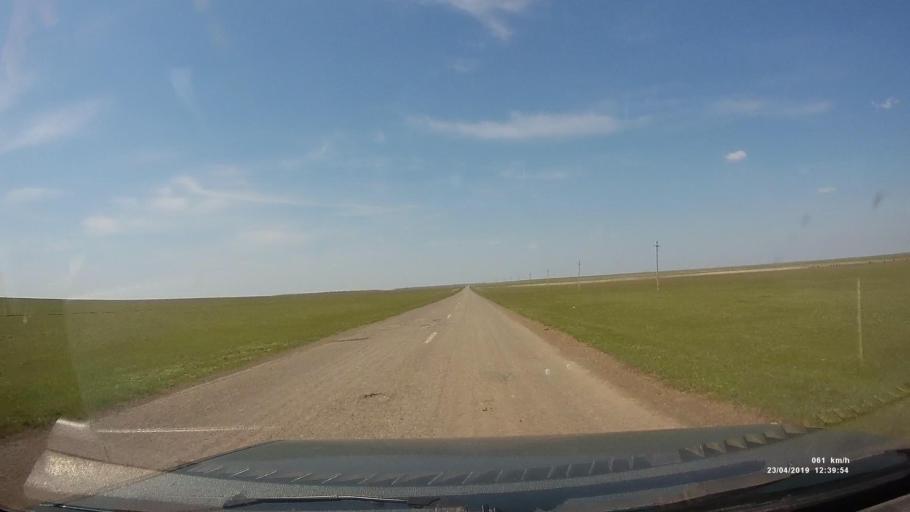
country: RU
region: Kalmykiya
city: Yashalta
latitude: 46.4367
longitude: 42.7038
